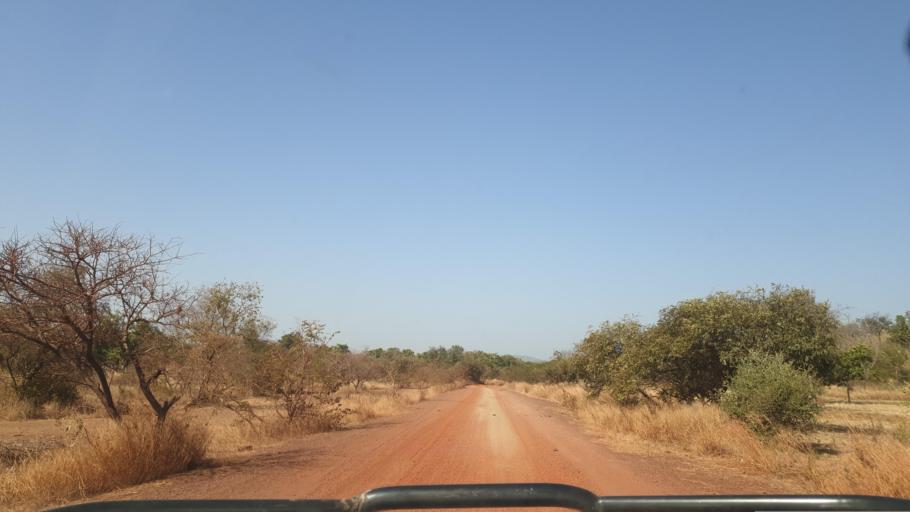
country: ML
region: Sikasso
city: Bougouni
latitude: 11.8207
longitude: -6.9626
